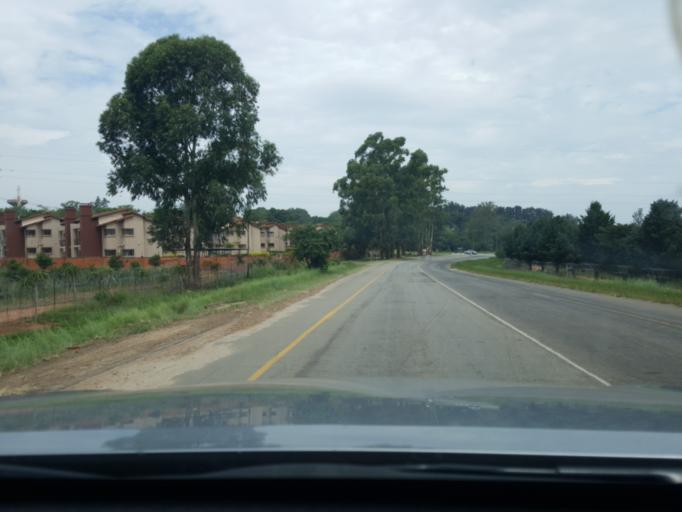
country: ZA
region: Mpumalanga
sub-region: Ehlanzeni District
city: White River
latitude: -25.3311
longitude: 30.9950
